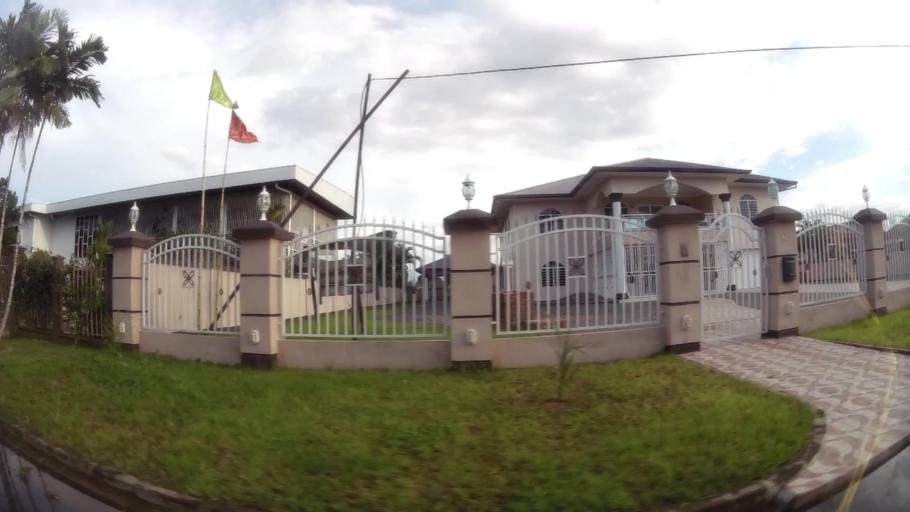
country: SR
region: Paramaribo
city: Paramaribo
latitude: 5.8367
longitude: -55.1867
